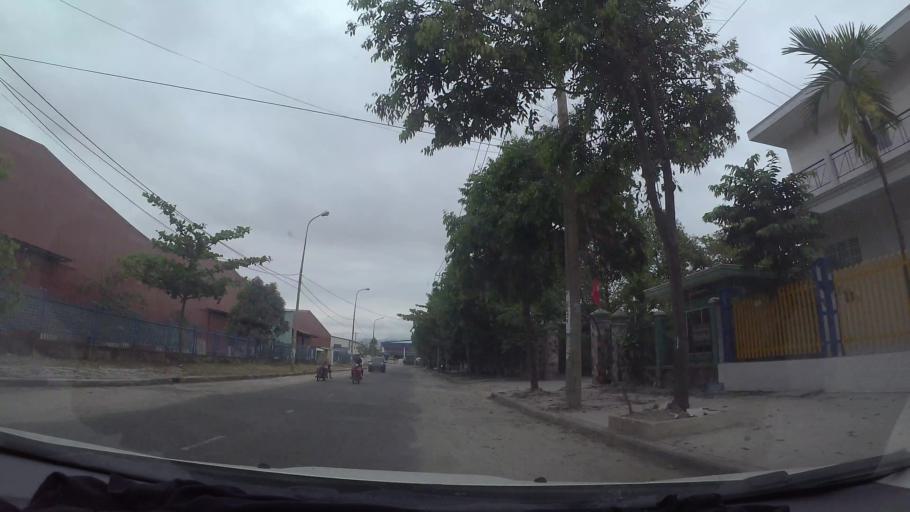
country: VN
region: Da Nang
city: Lien Chieu
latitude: 16.0864
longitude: 108.1379
